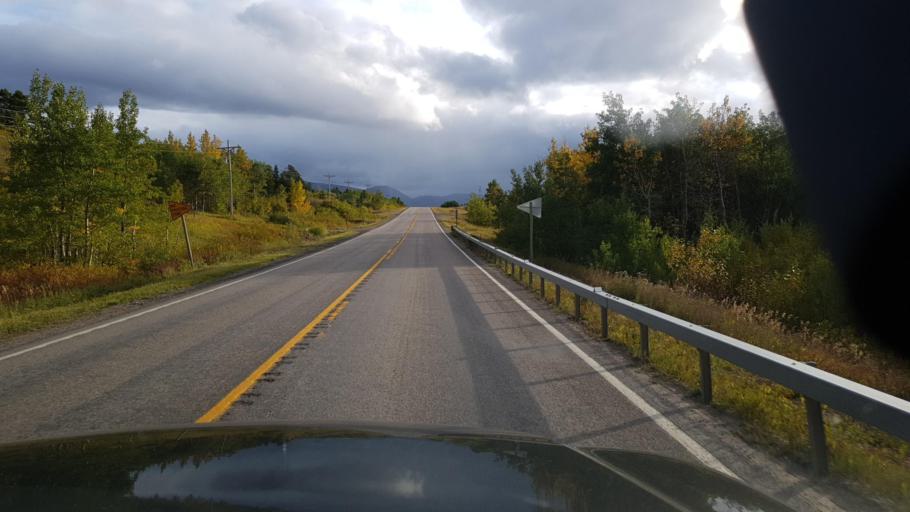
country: US
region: Montana
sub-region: Glacier County
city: South Browning
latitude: 48.3775
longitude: -113.2760
